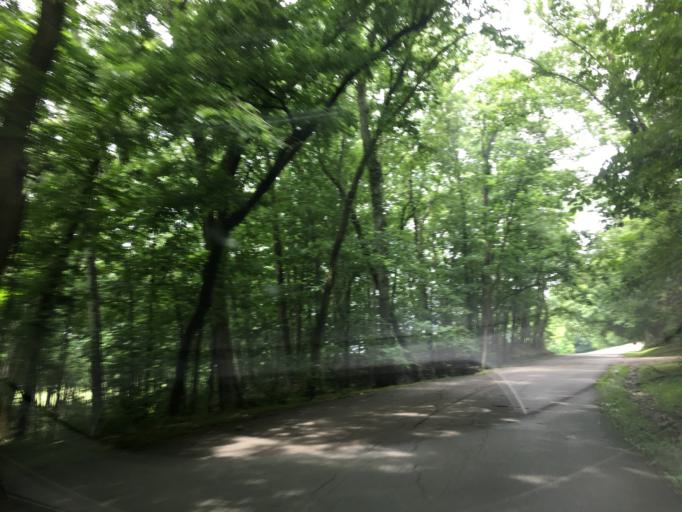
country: US
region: Tennessee
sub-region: Davidson County
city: Forest Hills
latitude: 36.0523
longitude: -86.9137
